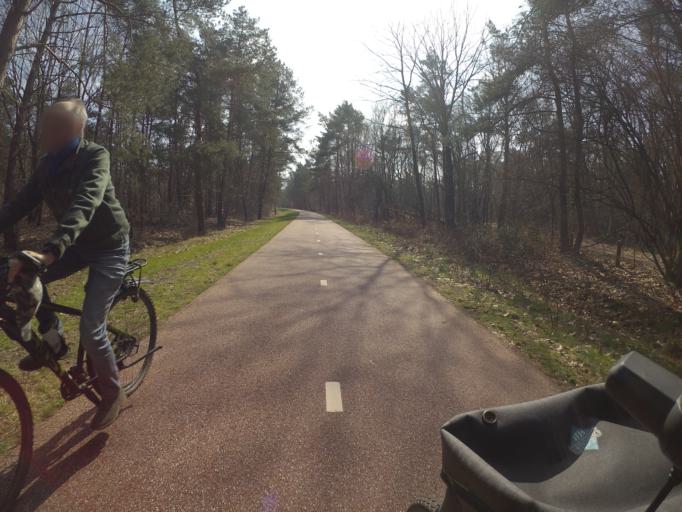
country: NL
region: North Brabant
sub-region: Gemeente Goirle
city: Goirle
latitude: 51.5525
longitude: 5.0211
